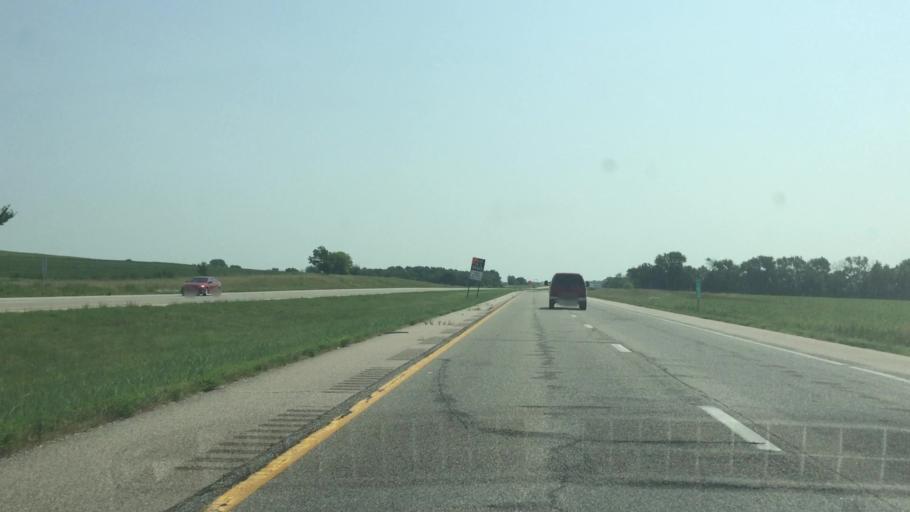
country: US
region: Kansas
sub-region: Osage County
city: Lyndon
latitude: 38.4266
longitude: -95.7742
